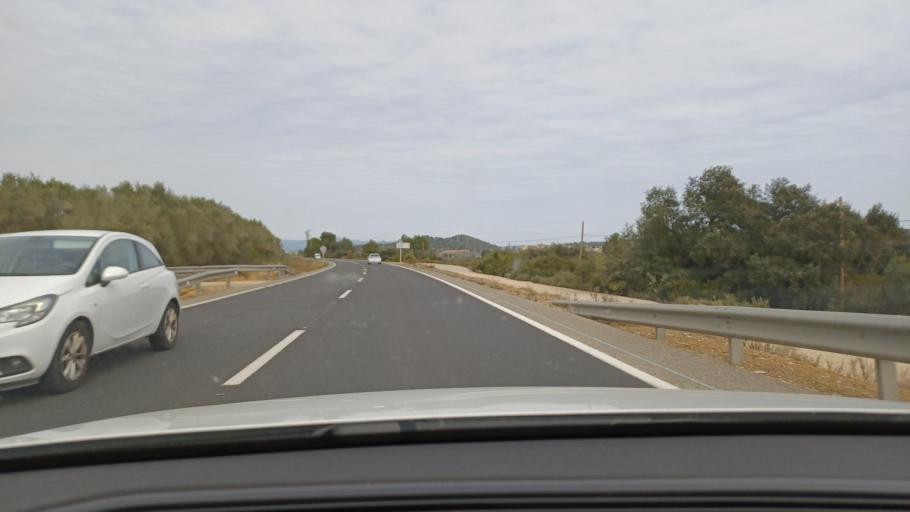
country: ES
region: Catalonia
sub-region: Provincia de Tarragona
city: Santa Barbara
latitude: 40.6556
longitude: 0.5073
